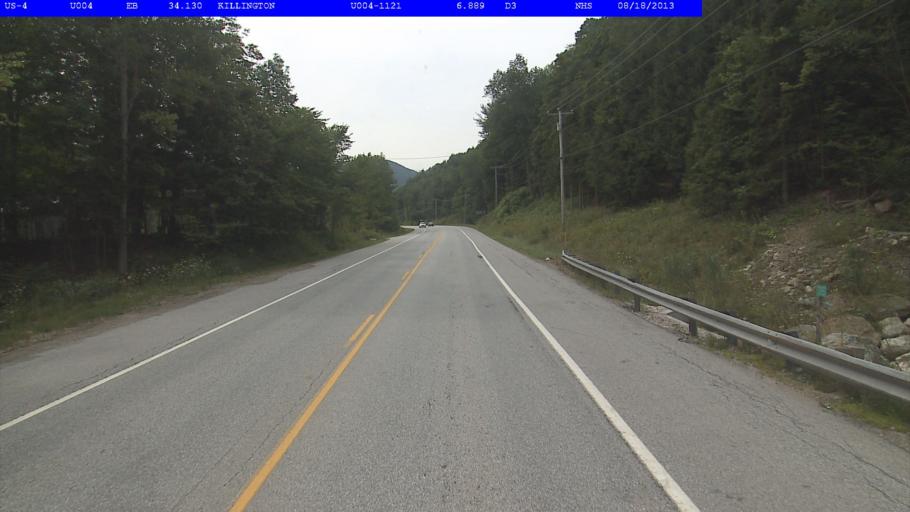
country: US
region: Vermont
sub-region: Rutland County
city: Rutland
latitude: 43.6216
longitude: -72.7600
